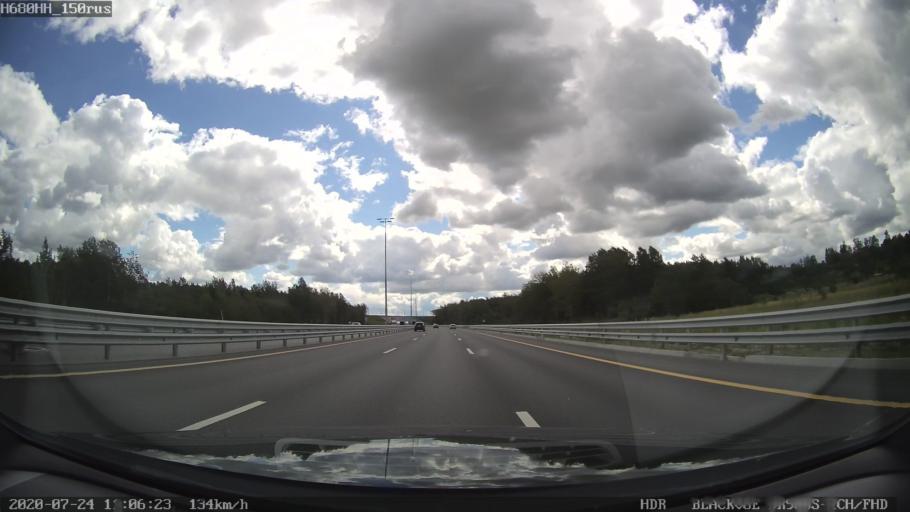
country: RU
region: St.-Petersburg
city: Shushary
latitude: 59.7638
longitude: 30.3740
